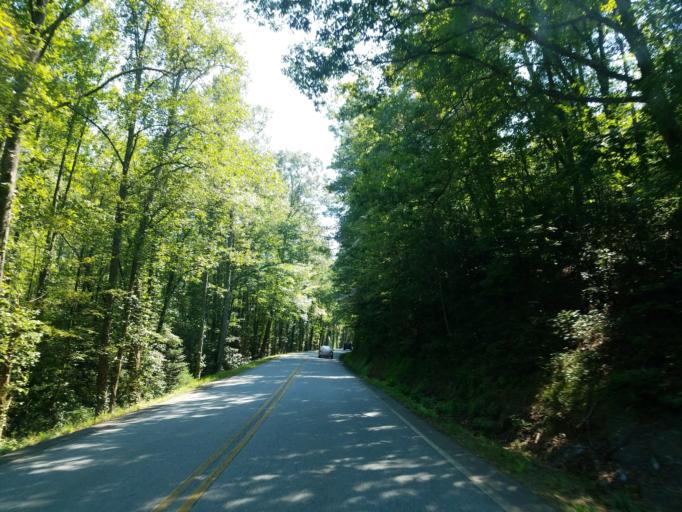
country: US
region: Georgia
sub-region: Lumpkin County
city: Dahlonega
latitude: 34.6315
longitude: -83.9356
